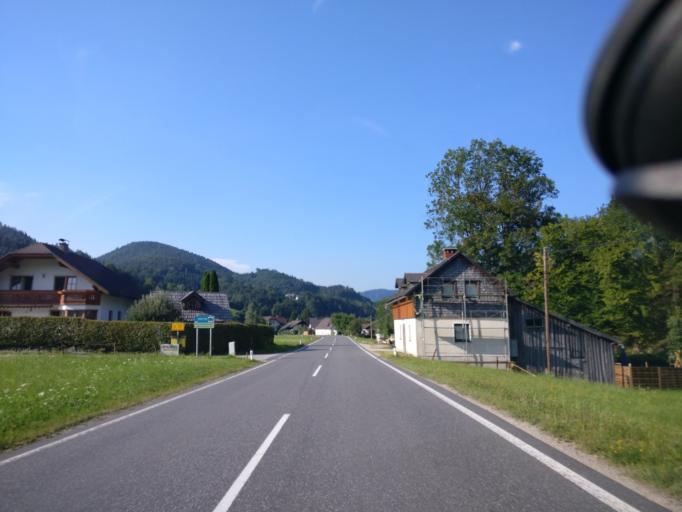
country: AT
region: Lower Austria
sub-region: Politischer Bezirk Scheibbs
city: Gostling an der Ybbs
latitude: 47.7884
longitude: 14.9176
